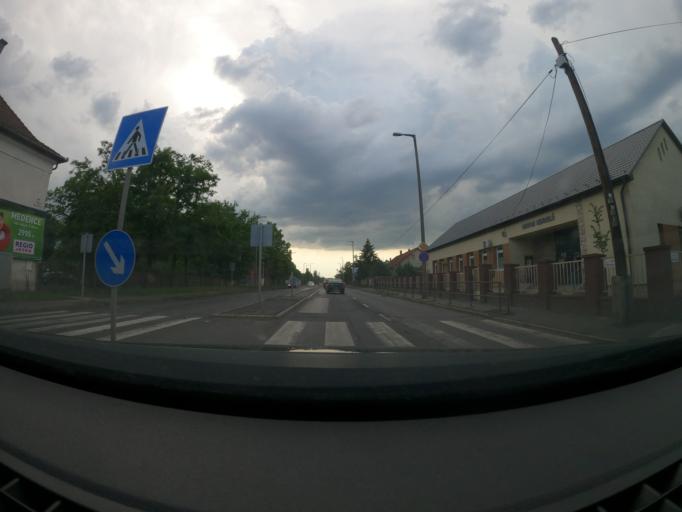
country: HU
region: Hajdu-Bihar
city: Debrecen
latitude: 47.5290
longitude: 21.6563
